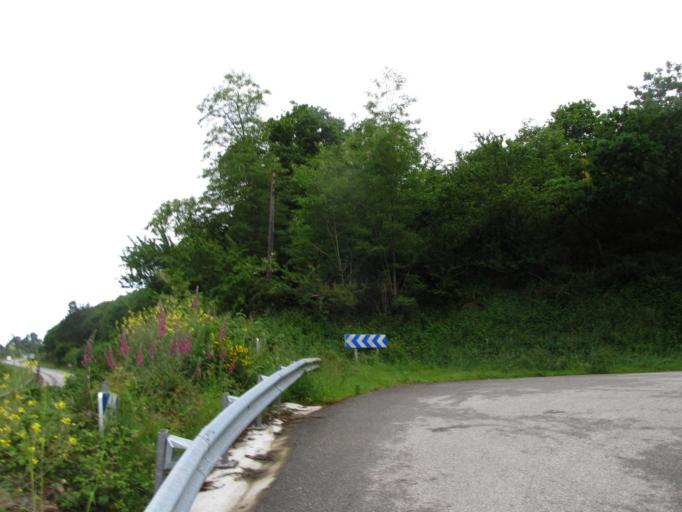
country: FR
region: Brittany
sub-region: Departement du Finistere
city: Plounevezel
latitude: 48.2851
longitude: -3.6013
